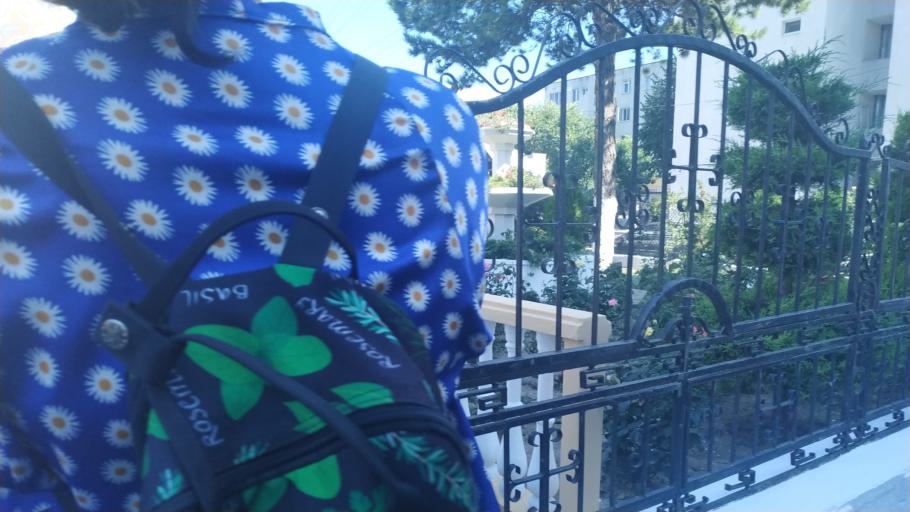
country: RO
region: Constanta
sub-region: Municipiul Constanta
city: Constanta
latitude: 44.1791
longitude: 28.6470
